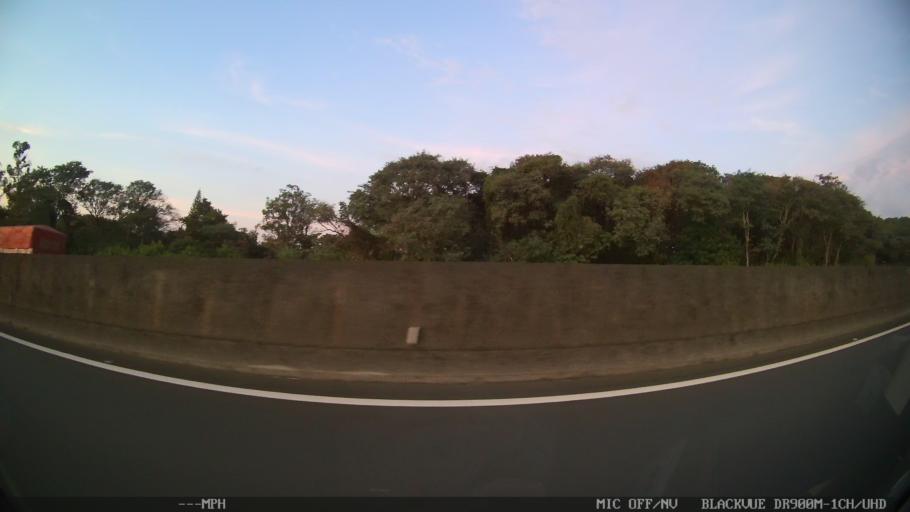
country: BR
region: Sao Paulo
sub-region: Valinhos
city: Valinhos
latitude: -22.9775
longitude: -47.0483
